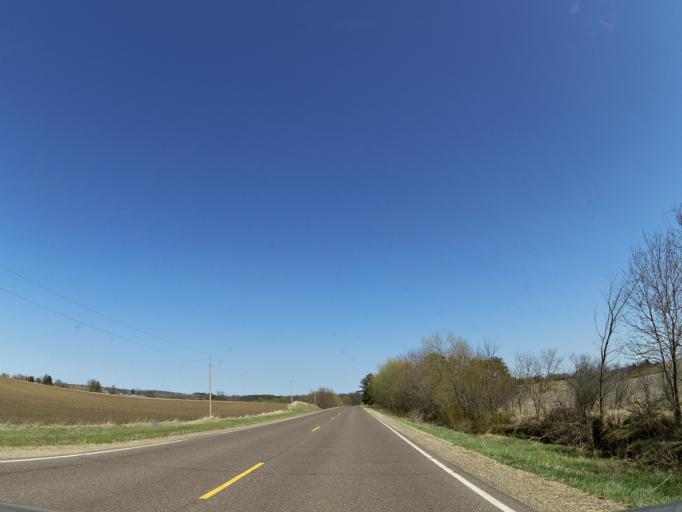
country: US
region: Wisconsin
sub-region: Saint Croix County
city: Baldwin
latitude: 44.8696
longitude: -92.4252
